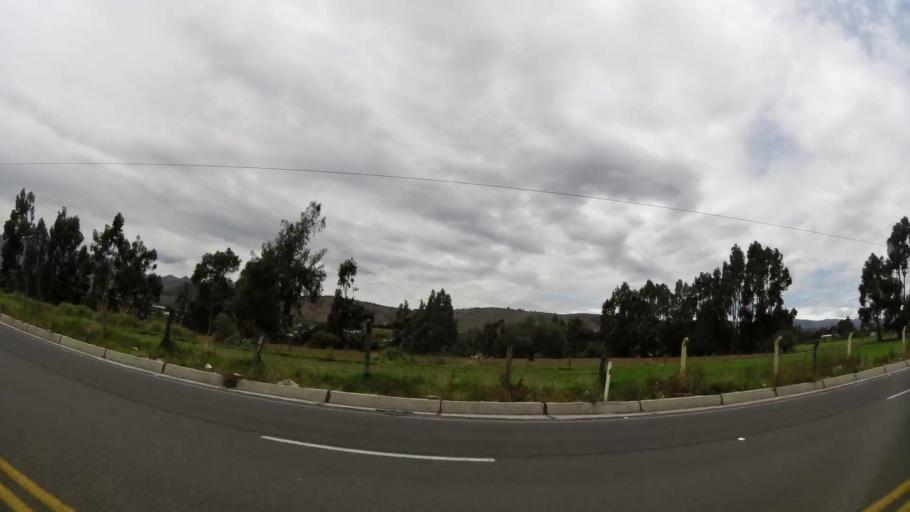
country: EC
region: Cotopaxi
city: San Miguel de Salcedo
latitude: -1.0099
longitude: -78.5931
